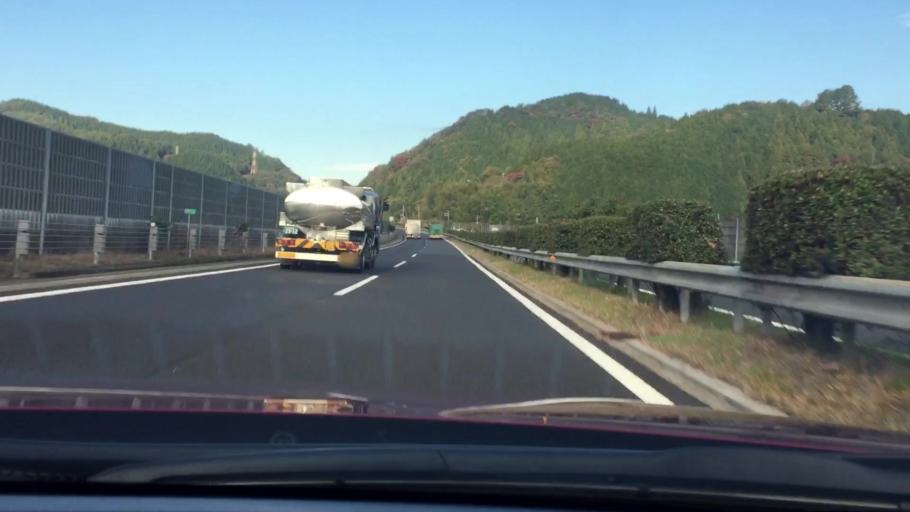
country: JP
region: Hyogo
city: Yamazakicho-nakabirose
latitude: 34.9775
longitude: 134.6341
